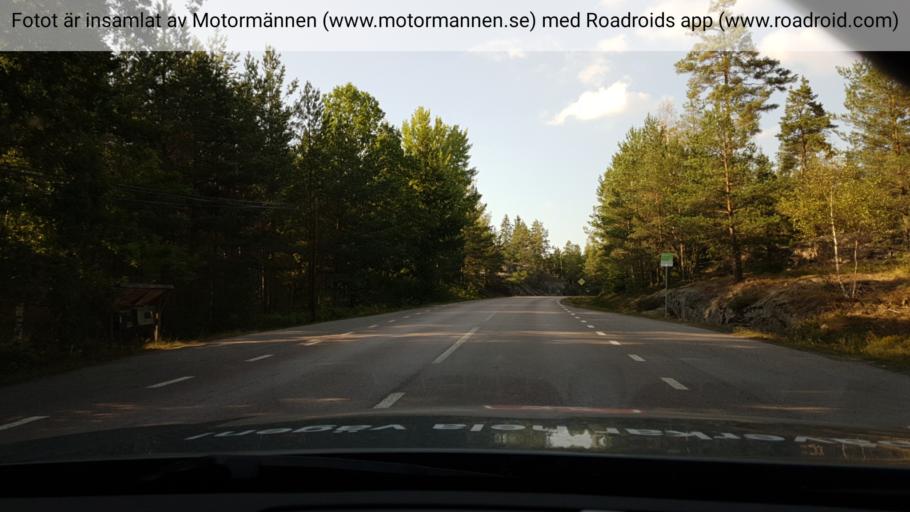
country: SE
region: Soedermanland
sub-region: Strangnas Kommun
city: Mariefred
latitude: 59.1793
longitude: 17.1893
